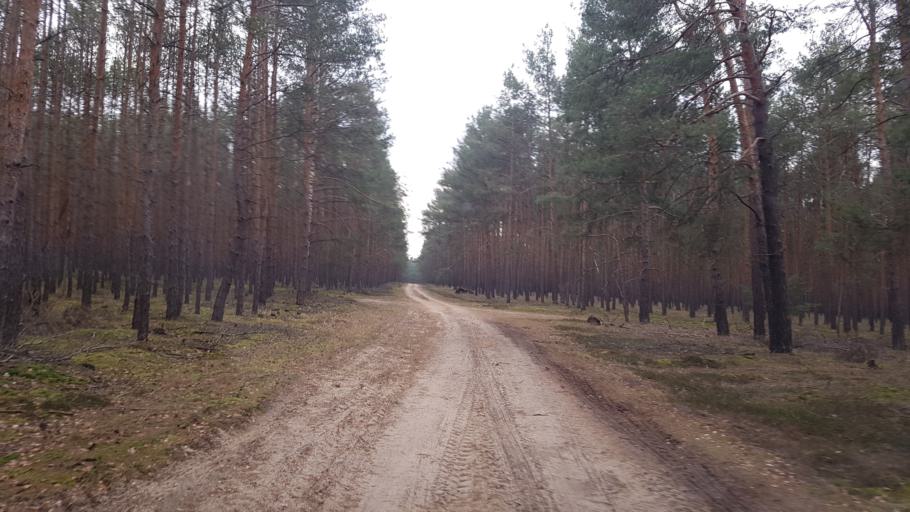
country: DE
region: Brandenburg
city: Schilda
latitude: 51.6250
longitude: 13.3863
